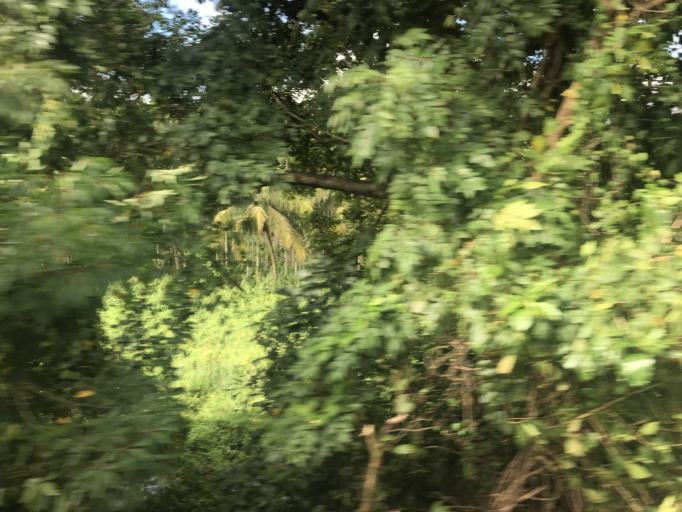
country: IN
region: Kerala
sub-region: Palakkad district
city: Palakkad
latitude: 10.8145
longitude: 76.6688
